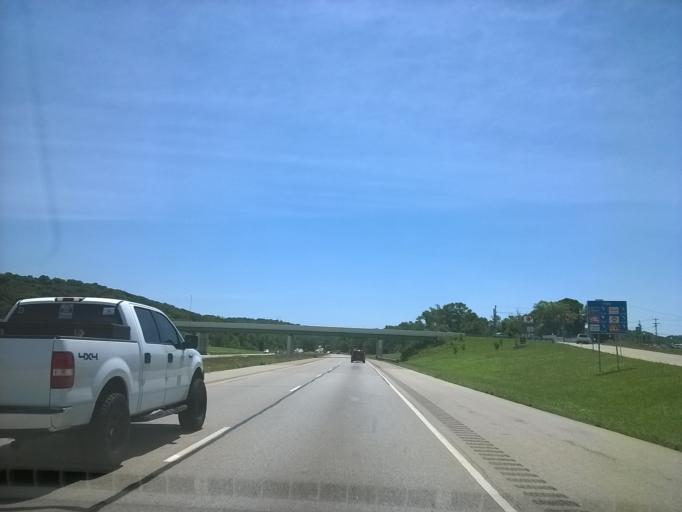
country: US
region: Ohio
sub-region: Hamilton County
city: Harrison
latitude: 39.2415
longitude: -84.7731
